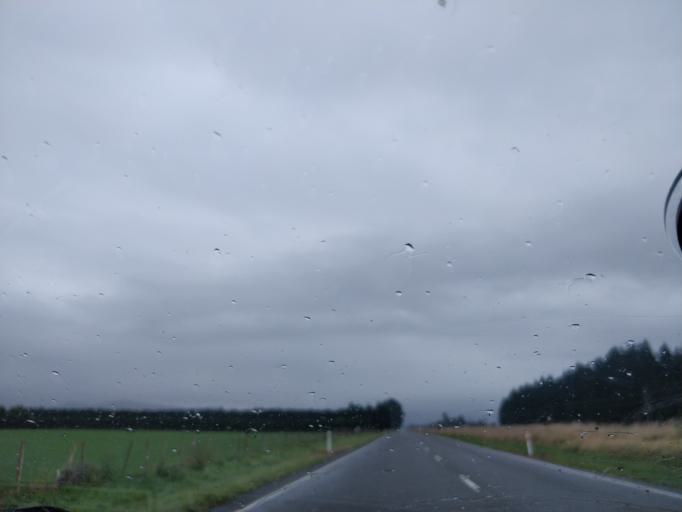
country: NZ
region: Canterbury
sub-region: Selwyn District
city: Darfield
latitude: -43.3805
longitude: 172.0048
